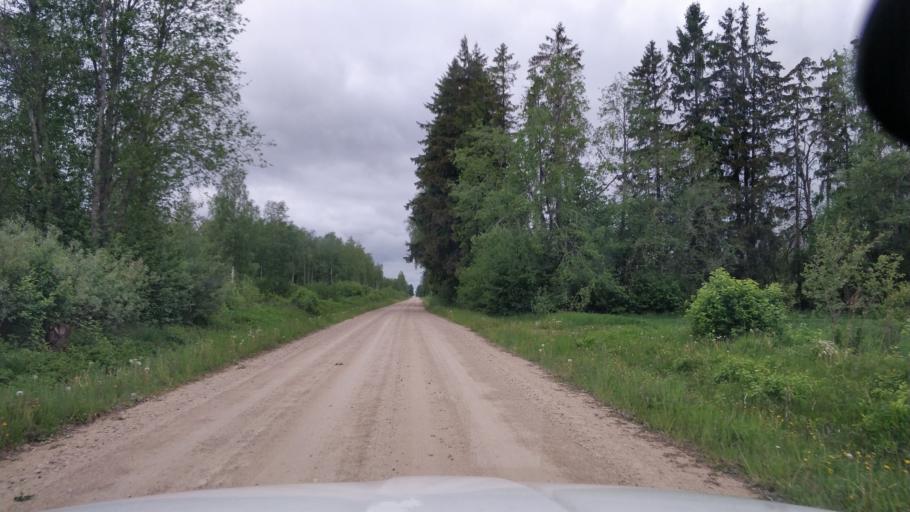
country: EE
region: Raplamaa
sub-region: Maerjamaa vald
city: Marjamaa
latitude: 58.7175
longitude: 24.2923
